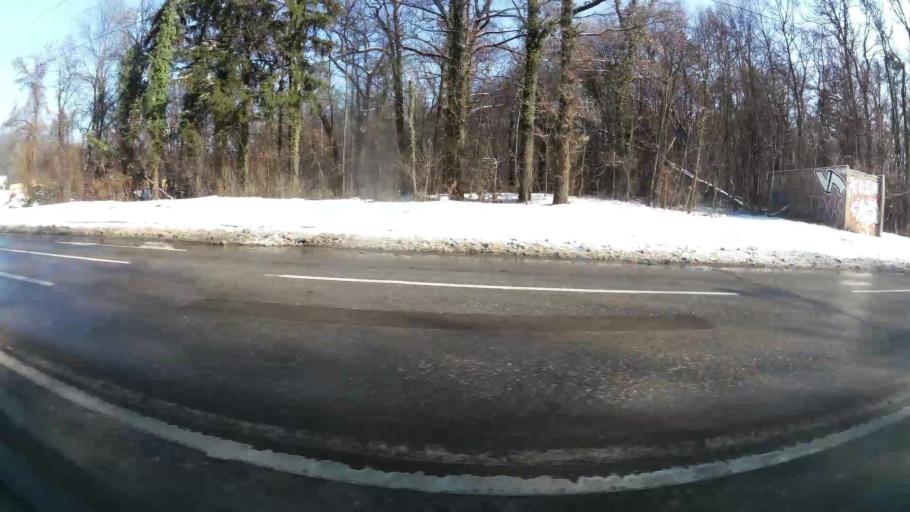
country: BG
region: Sofia-Capital
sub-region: Stolichna Obshtina
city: Sofia
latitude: 42.6662
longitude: 23.3374
